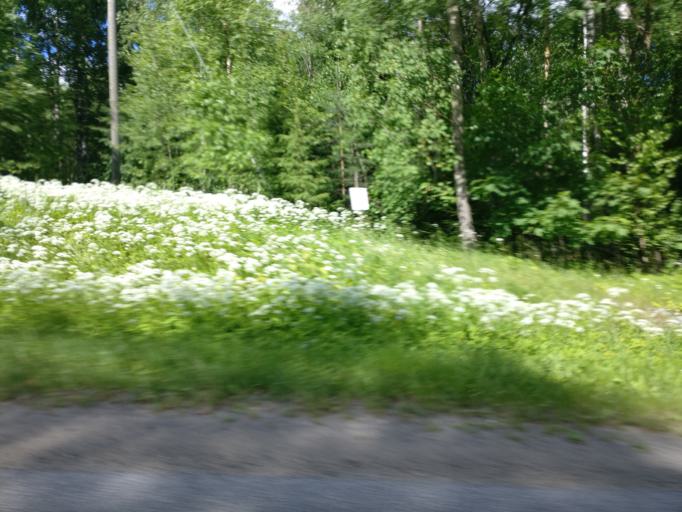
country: FI
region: Southern Savonia
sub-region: Savonlinna
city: Kerimaeki
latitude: 61.8826
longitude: 29.1046
